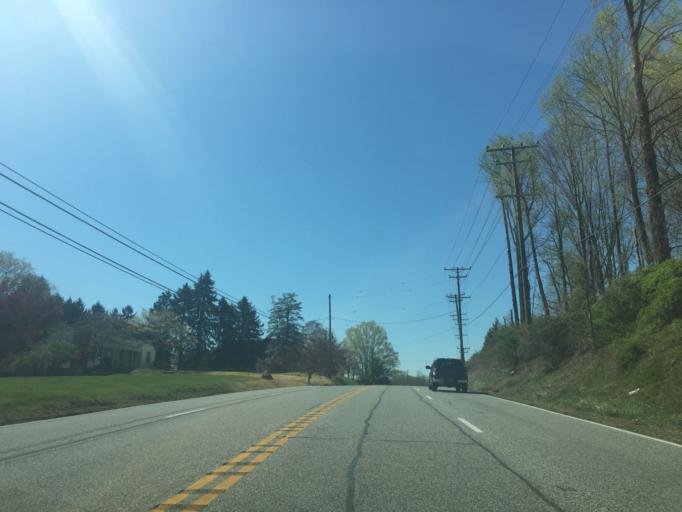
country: US
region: Maryland
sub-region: Baltimore County
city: Kingsville
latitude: 39.4671
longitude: -76.4104
